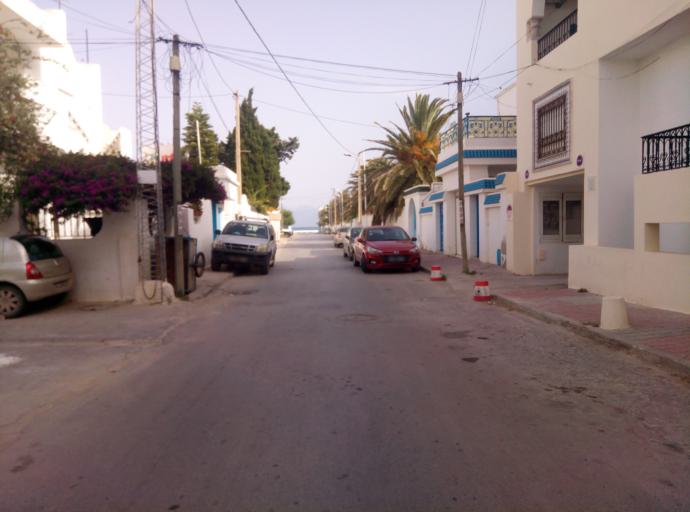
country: TN
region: Nabul
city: Al Hammamat
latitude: 36.3951
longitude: 10.6172
